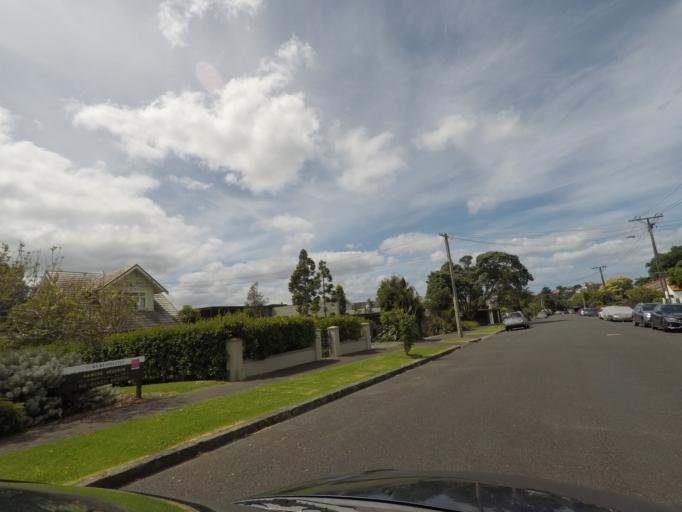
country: NZ
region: Auckland
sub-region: Auckland
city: Auckland
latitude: -36.8520
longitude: 174.7184
